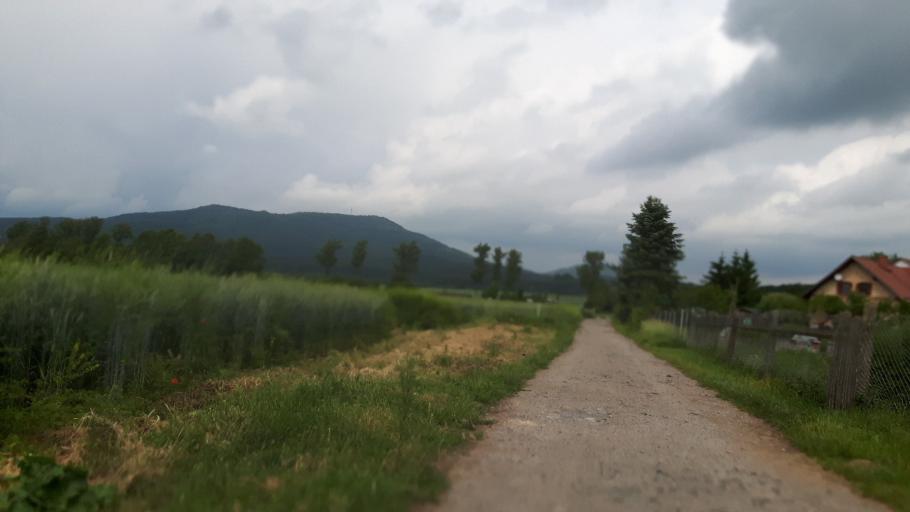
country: DE
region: Thuringia
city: Gleichamberg
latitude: 50.3629
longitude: 10.6315
